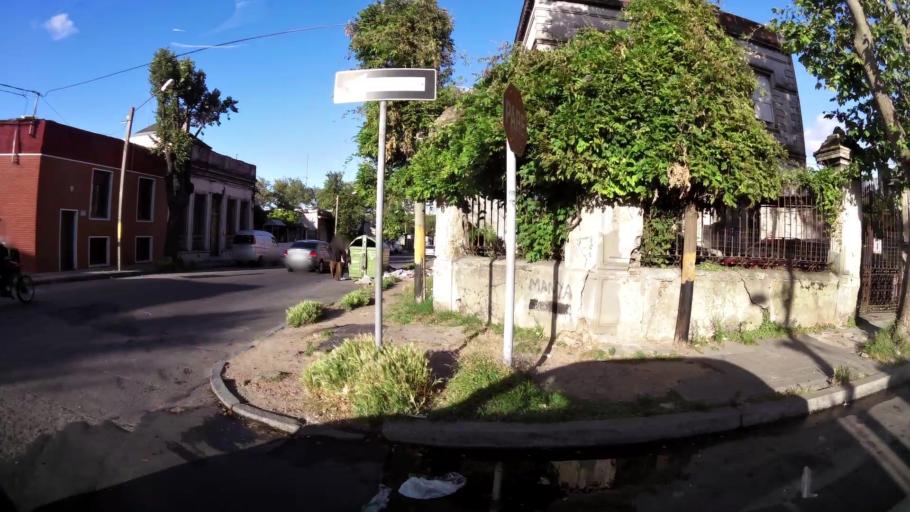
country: UY
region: Montevideo
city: Montevideo
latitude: -34.8741
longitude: -56.1428
